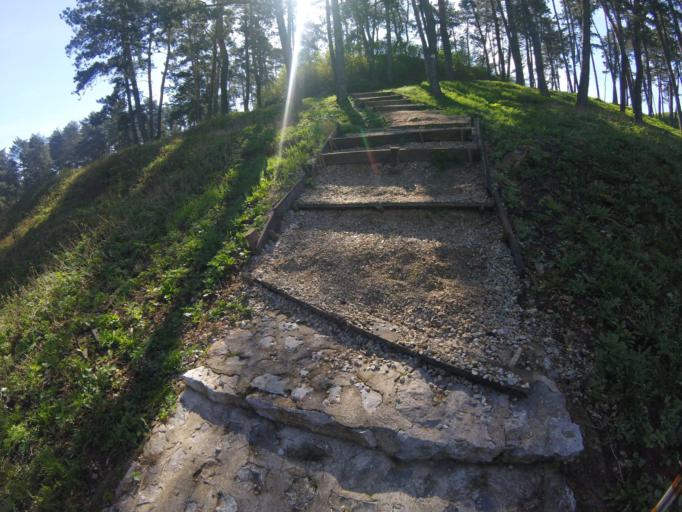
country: HU
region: Borsod-Abauj-Zemplen
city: Szendro
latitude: 48.4086
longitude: 20.7337
